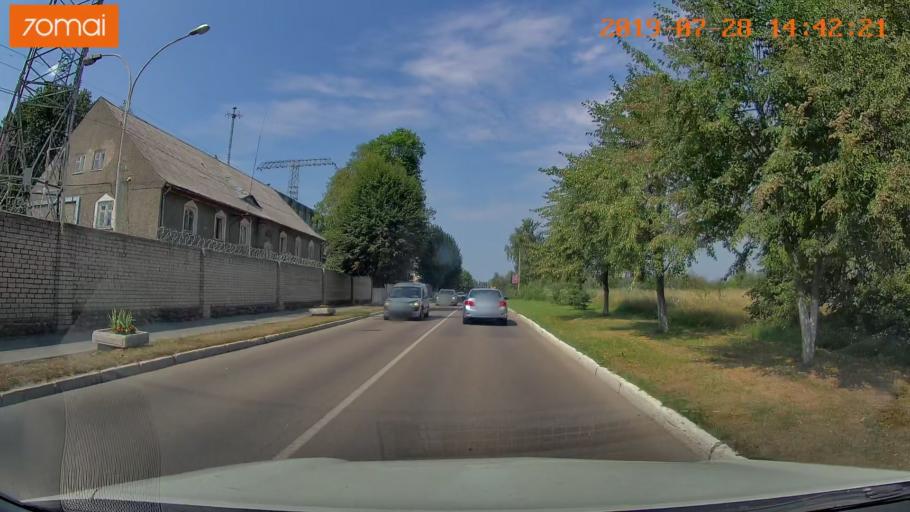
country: RU
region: Kaliningrad
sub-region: Gorod Kaliningrad
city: Yantarnyy
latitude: 54.8594
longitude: 19.9425
